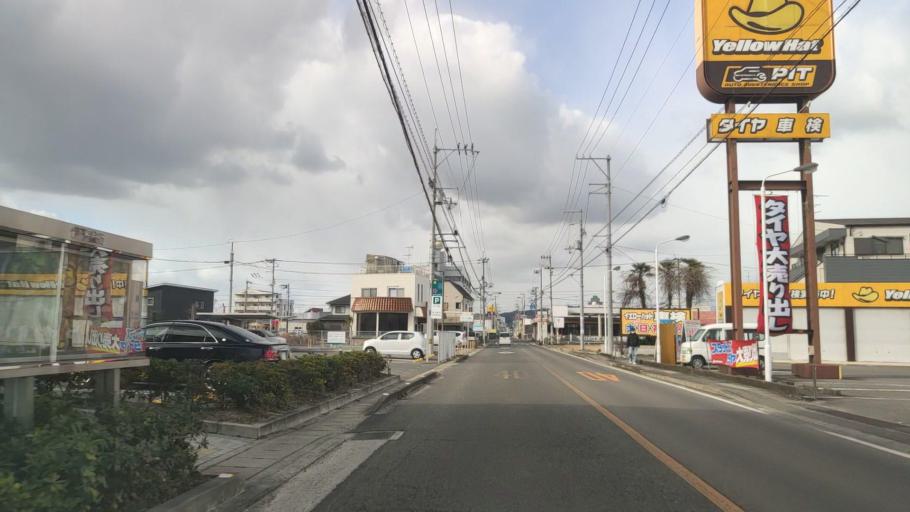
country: JP
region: Ehime
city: Saijo
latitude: 34.0506
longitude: 133.0137
